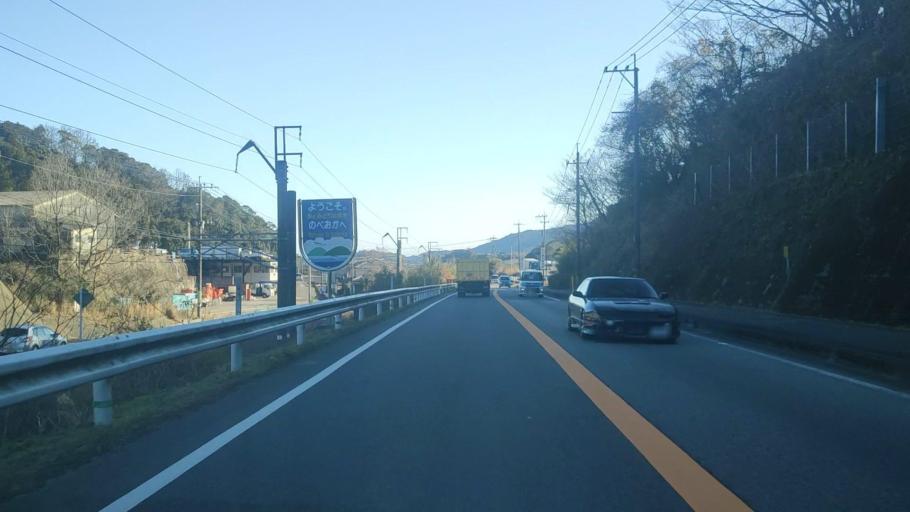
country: JP
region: Miyazaki
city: Nobeoka
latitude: 32.5026
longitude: 131.6659
